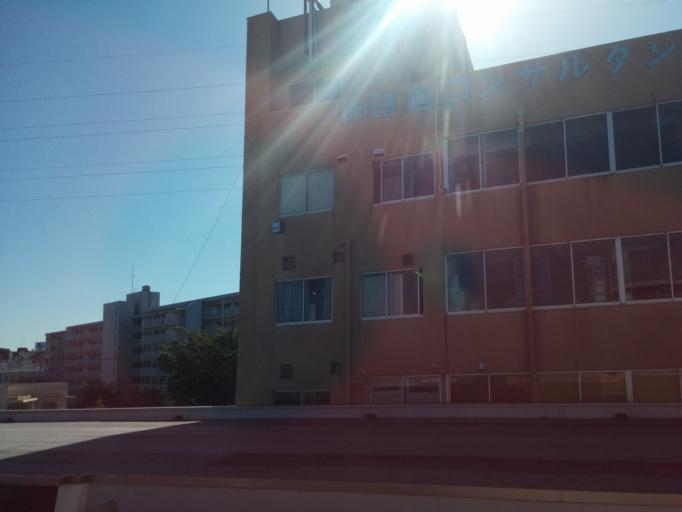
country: JP
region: Kanagawa
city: Yokohama
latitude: 35.5150
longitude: 139.6270
